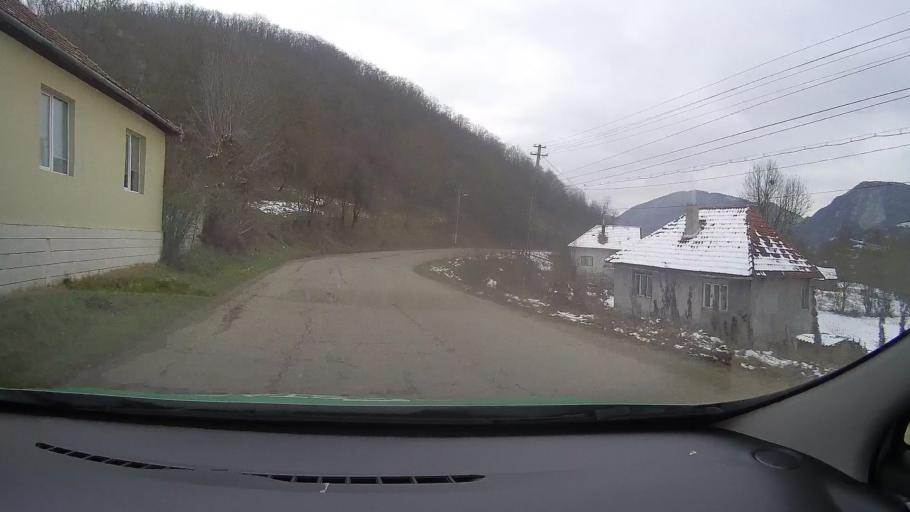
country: RO
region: Hunedoara
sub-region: Comuna Balsa
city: Balsa
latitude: 46.0279
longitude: 23.1026
